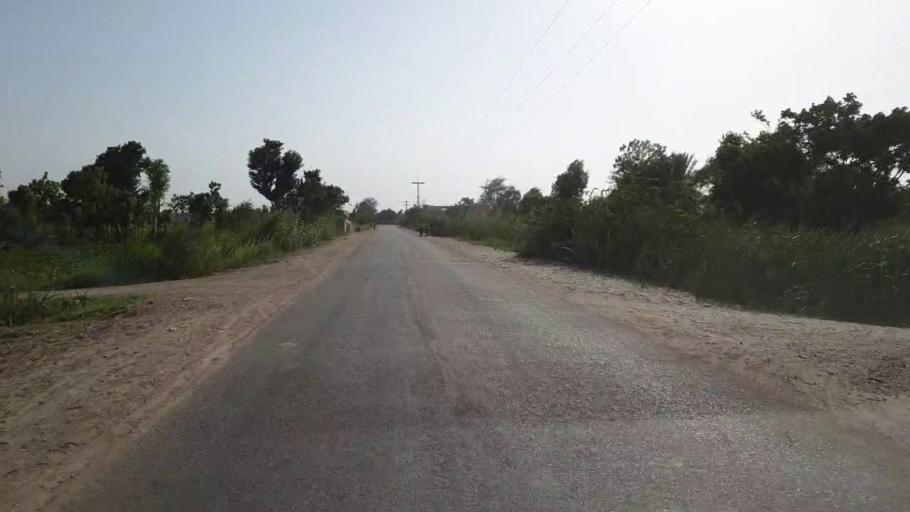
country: PK
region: Sindh
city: Daur
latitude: 26.4743
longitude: 68.4573
